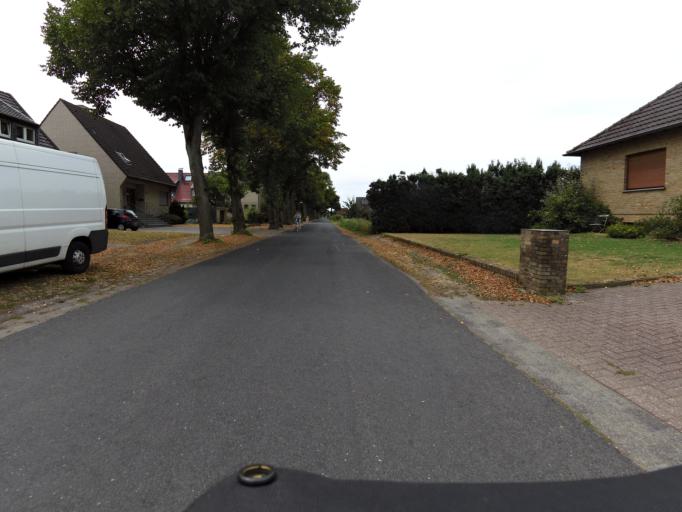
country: DE
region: North Rhine-Westphalia
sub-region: Regierungsbezirk Dusseldorf
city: Kevelaer
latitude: 51.5681
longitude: 6.2516
